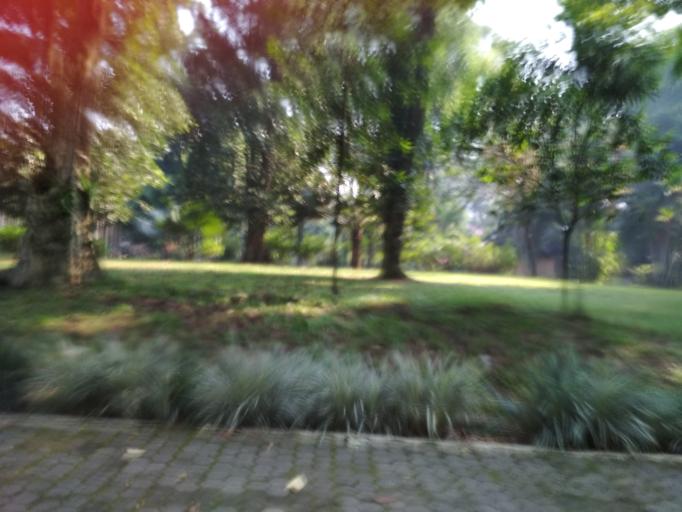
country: ID
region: West Java
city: Ciampea
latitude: -6.5608
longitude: 106.7269
